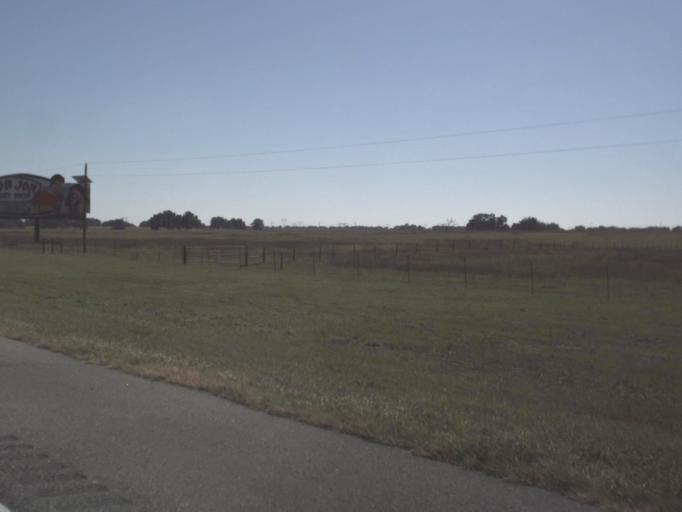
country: US
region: Florida
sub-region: Sumter County
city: Wildwood
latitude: 28.7844
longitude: -81.9796
